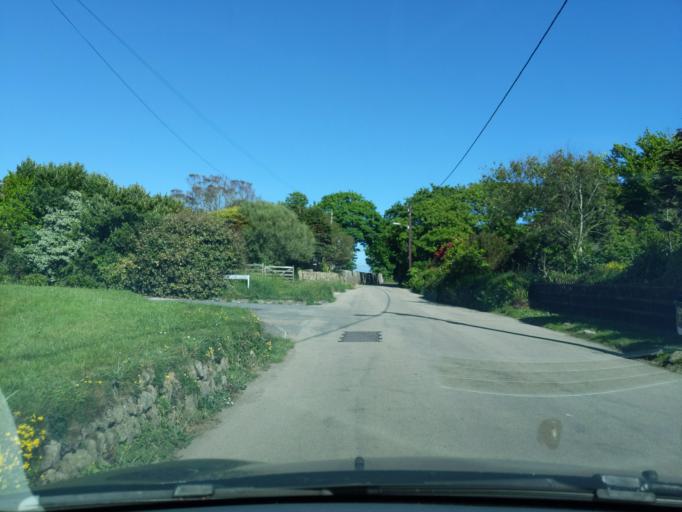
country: GB
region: England
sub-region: Cornwall
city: St. Buryan
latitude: 50.0742
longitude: -5.6207
